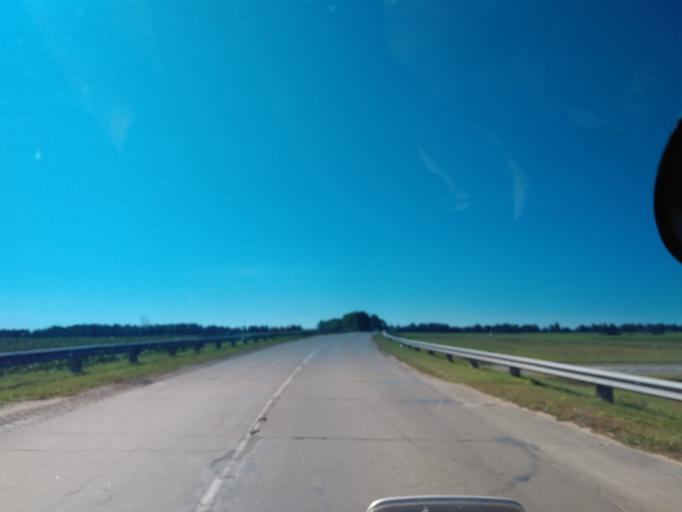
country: BY
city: Fanipol
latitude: 53.6925
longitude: 27.3605
